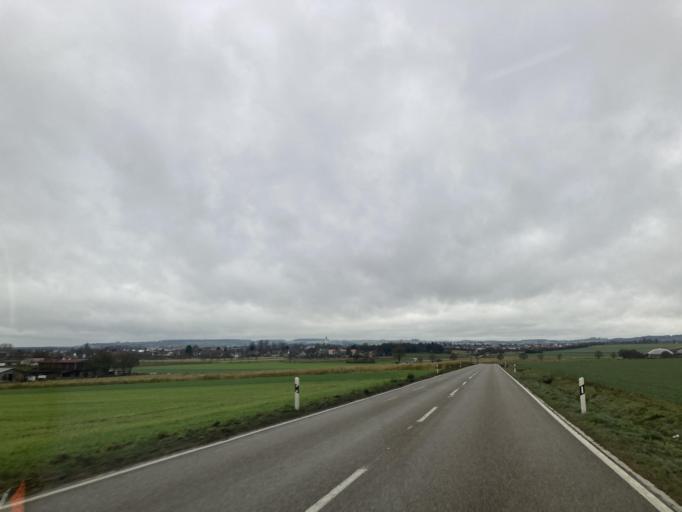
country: DE
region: Baden-Wuerttemberg
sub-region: Tuebingen Region
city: Ollingen
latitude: 48.5108
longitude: 10.1506
